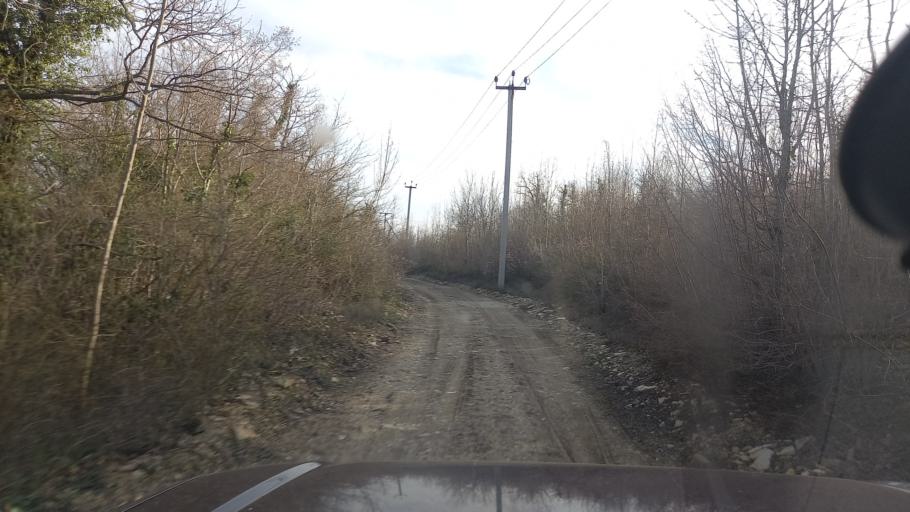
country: RU
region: Krasnodarskiy
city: Arkhipo-Osipovka
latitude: 44.3616
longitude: 38.5643
